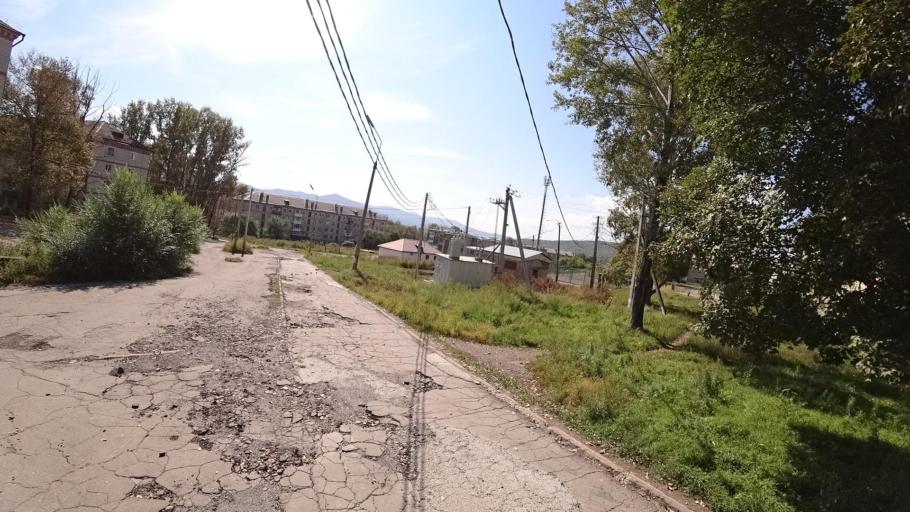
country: RU
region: Jewish Autonomous Oblast
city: Londoko
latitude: 49.0146
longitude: 131.8865
